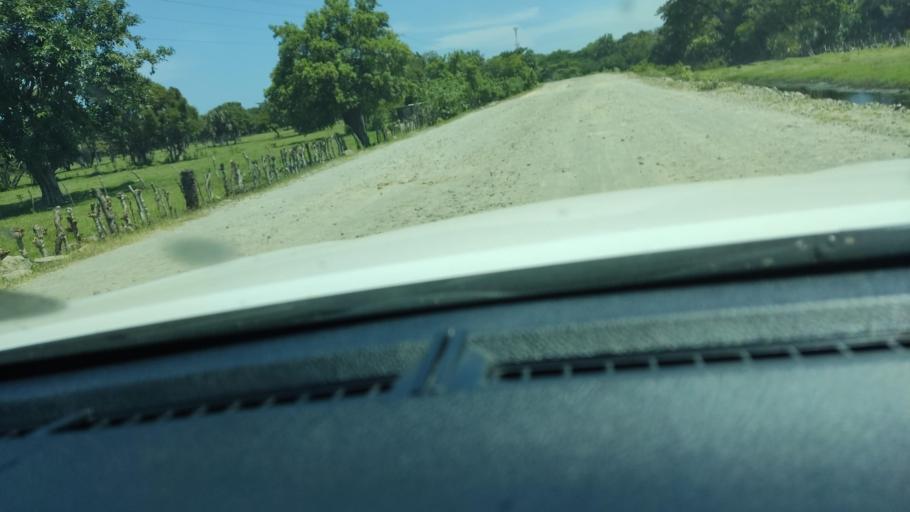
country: SV
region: Ahuachapan
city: San Francisco Menendez
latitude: 13.7585
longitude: -90.1188
